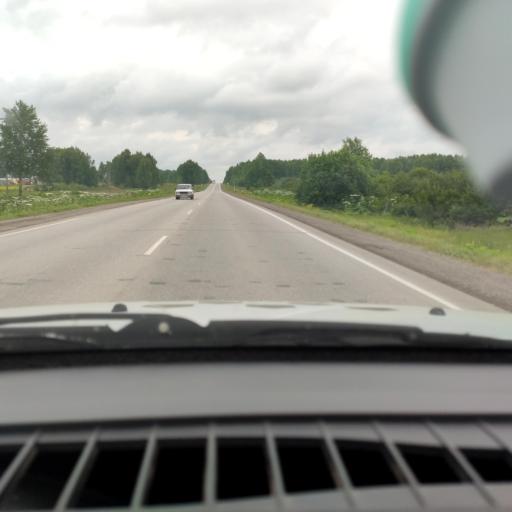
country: RU
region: Perm
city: Kungur
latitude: 57.4518
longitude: 57.0152
